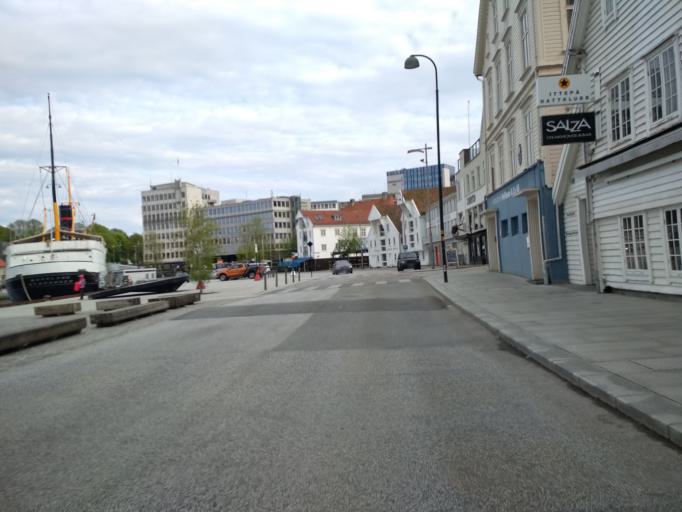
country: NO
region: Rogaland
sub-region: Stavanger
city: Stavanger
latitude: 58.9712
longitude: 5.7283
